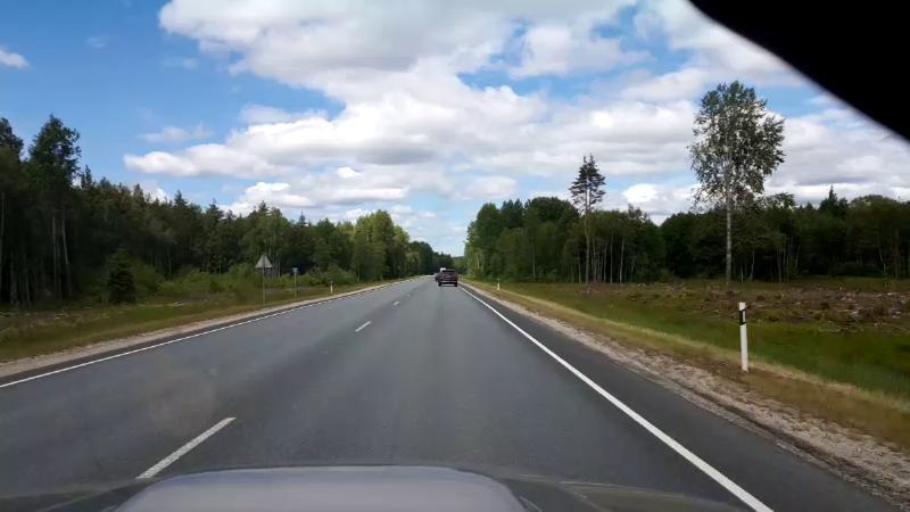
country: EE
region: Raplamaa
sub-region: Maerjamaa vald
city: Marjamaa
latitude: 59.0407
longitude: 24.4432
